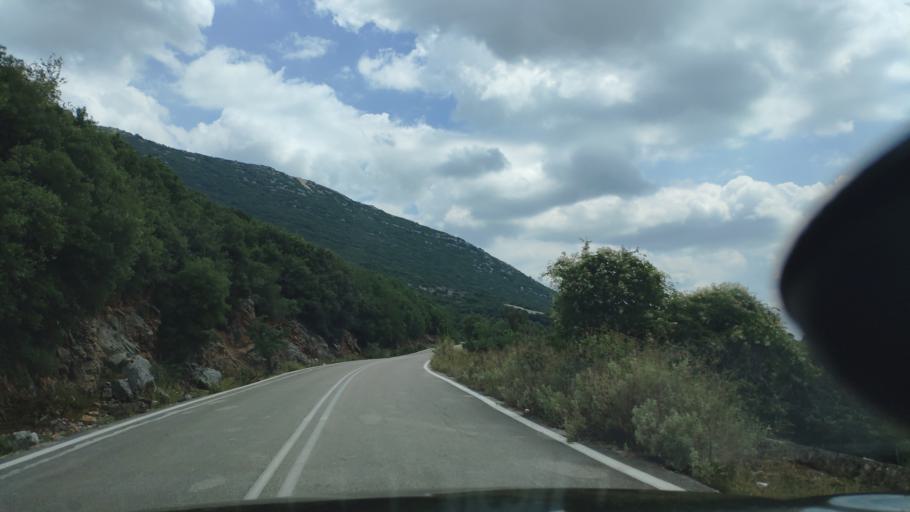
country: GR
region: Epirus
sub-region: Nomos Artas
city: Kampi
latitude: 39.2755
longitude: 20.9553
